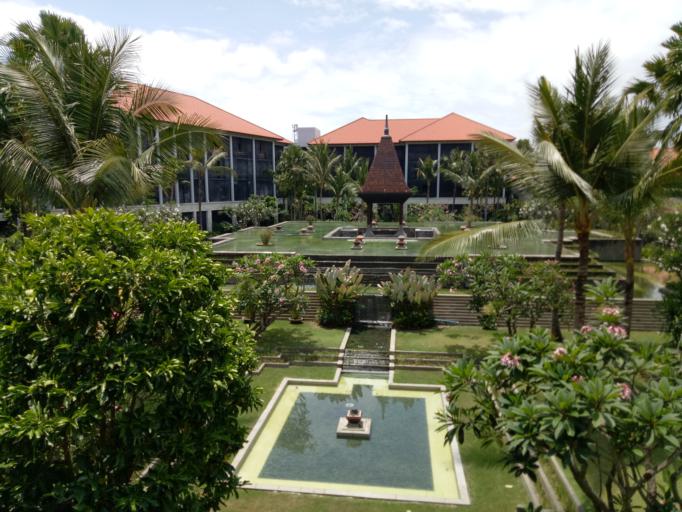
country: ID
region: Bali
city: Banjar Medura
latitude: -8.7059
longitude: 115.2625
